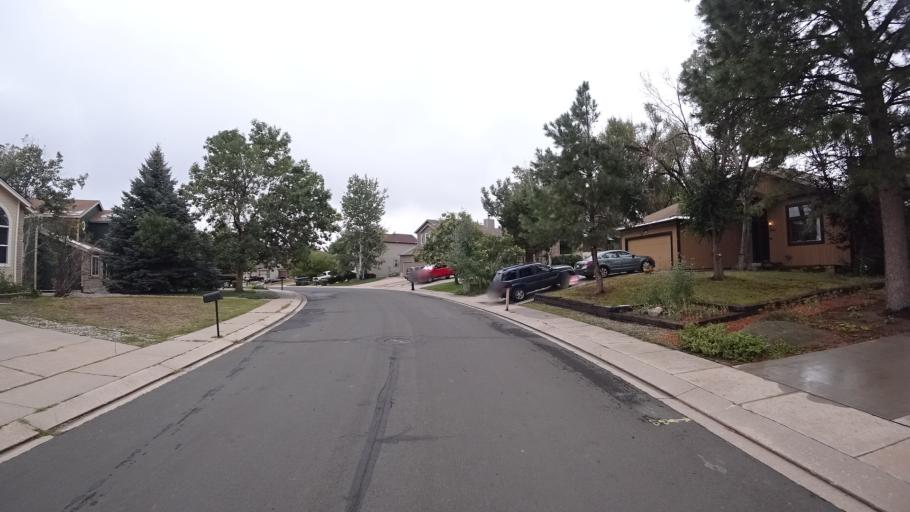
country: US
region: Colorado
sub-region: El Paso County
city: Cimarron Hills
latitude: 38.9194
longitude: -104.7575
